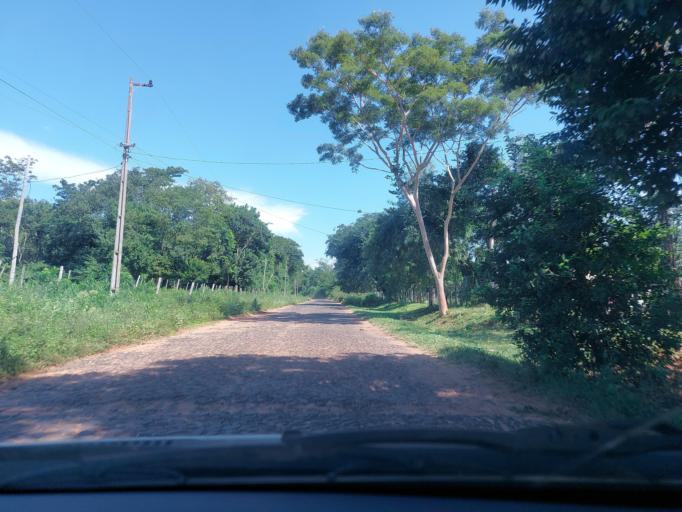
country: PY
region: San Pedro
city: Itacurubi del Rosario
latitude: -24.5761
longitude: -56.5993
